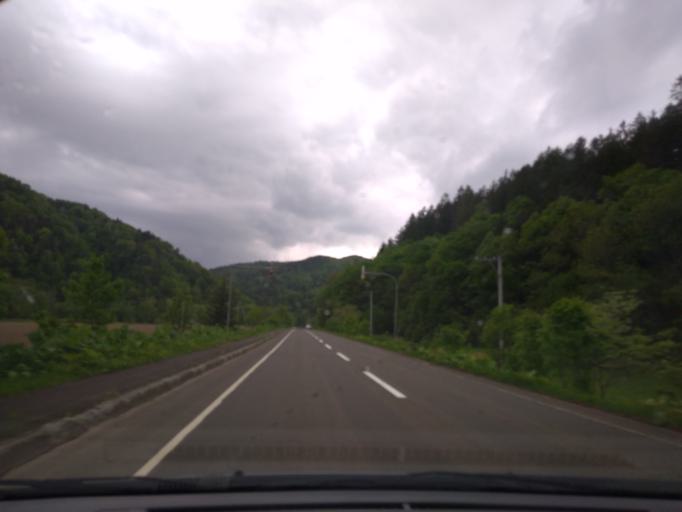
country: JP
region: Hokkaido
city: Shimo-furano
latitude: 43.1244
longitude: 142.4061
